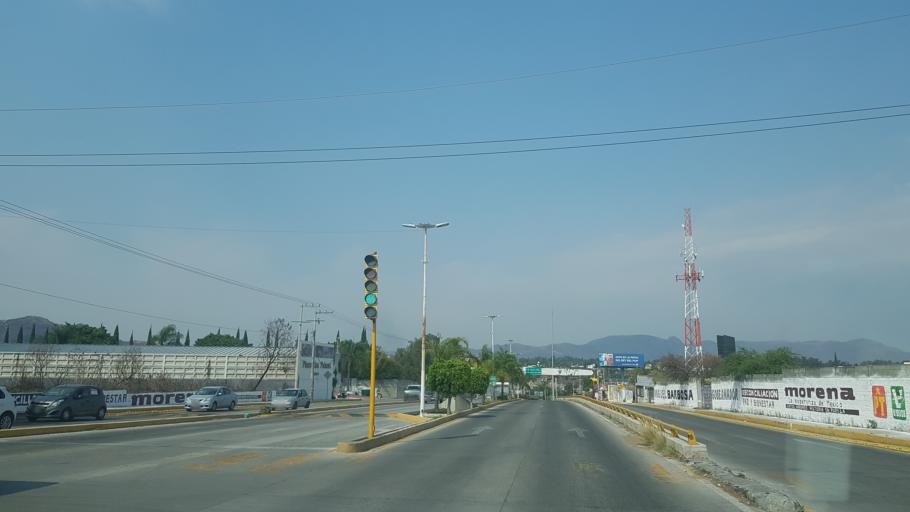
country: MX
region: Puebla
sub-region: Atlixco
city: El Encanto del Cerril
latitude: 18.9235
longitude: -98.4137
